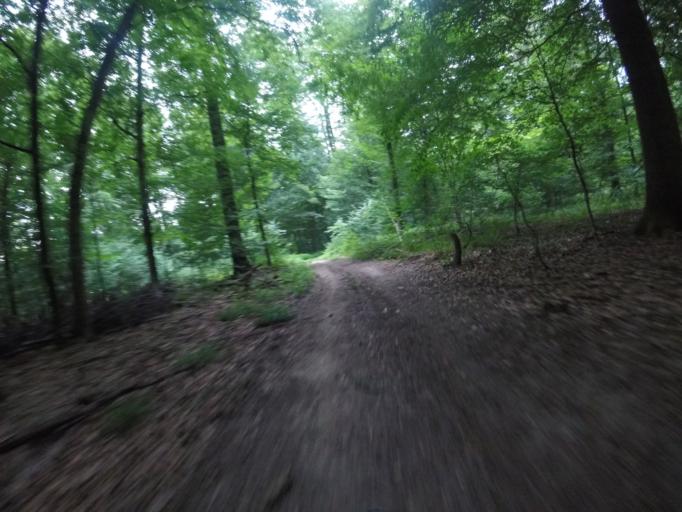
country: DE
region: Baden-Wuerttemberg
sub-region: Regierungsbezirk Stuttgart
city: Backnang
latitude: 48.9650
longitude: 9.4357
